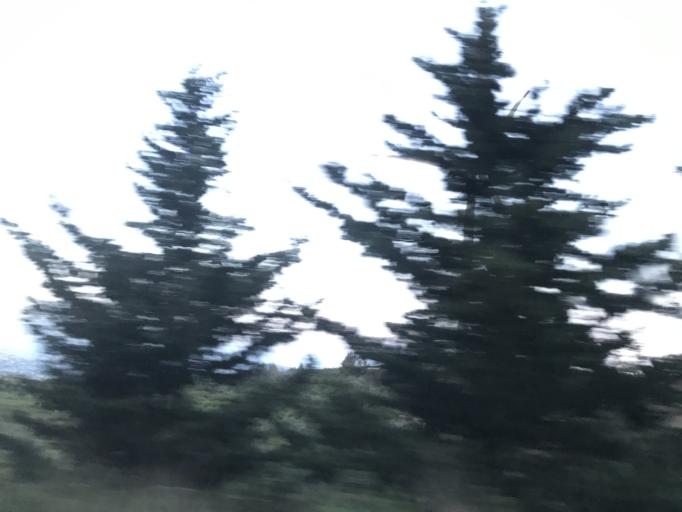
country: TR
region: Hatay
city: Buyukcat
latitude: 36.1035
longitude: 36.0433
